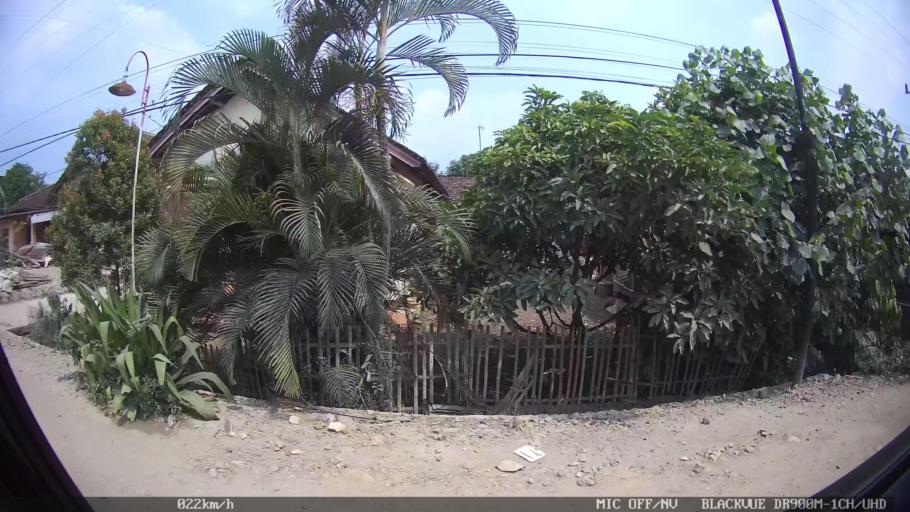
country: ID
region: Lampung
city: Gadingrejo
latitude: -5.3775
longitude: 105.0525
